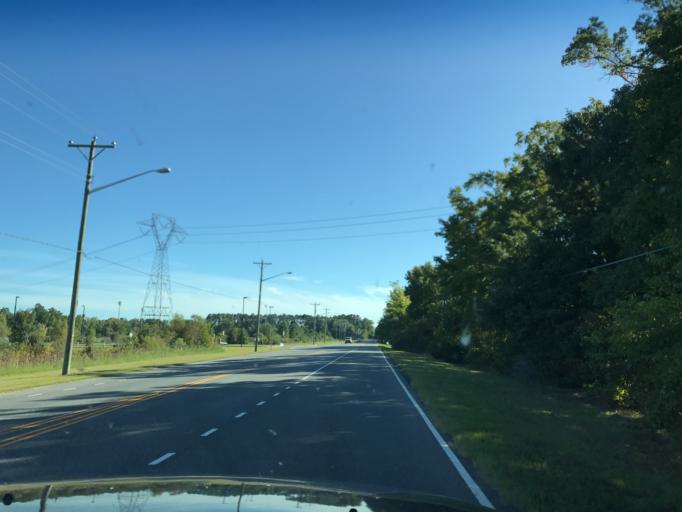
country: US
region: Virginia
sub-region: City of Portsmouth
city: Portsmouth Heights
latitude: 36.7235
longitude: -76.3495
